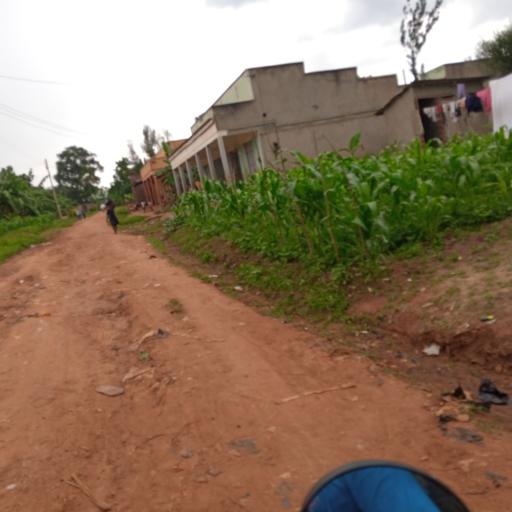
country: UG
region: Eastern Region
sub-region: Mbale District
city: Mbale
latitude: 1.1245
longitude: 34.1729
